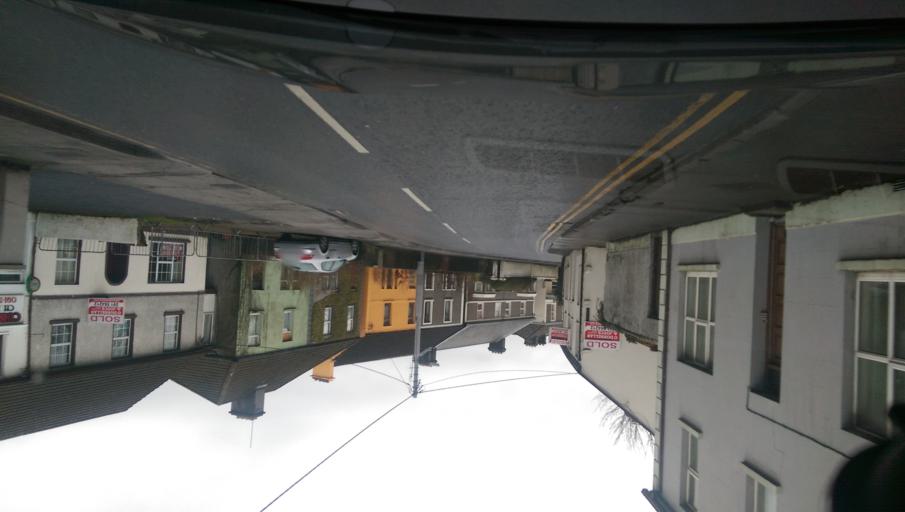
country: IE
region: Connaught
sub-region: County Galway
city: Gaillimh
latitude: 53.2725
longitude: -9.0625
